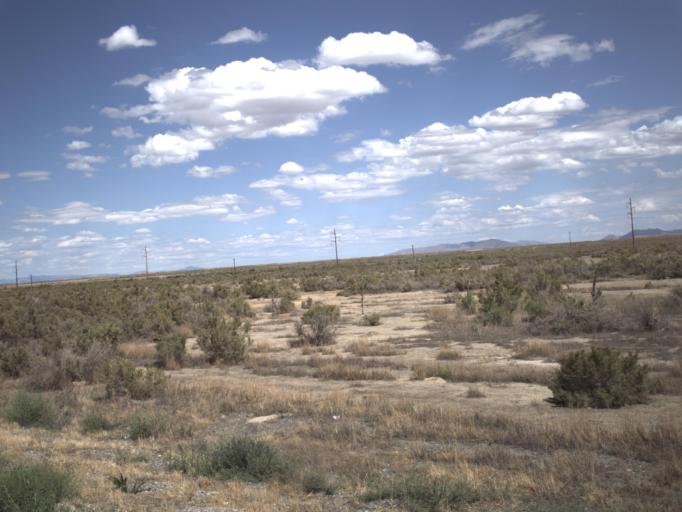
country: US
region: Utah
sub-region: Millard County
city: Delta
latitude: 39.2824
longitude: -112.4611
